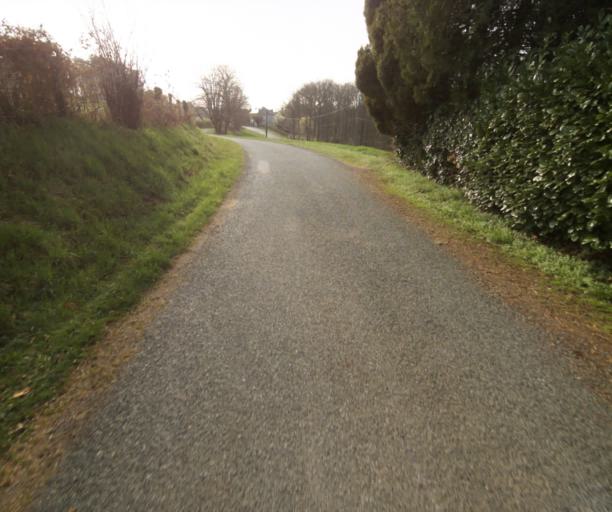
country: FR
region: Limousin
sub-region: Departement de la Correze
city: Chamboulive
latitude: 45.4338
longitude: 1.7640
